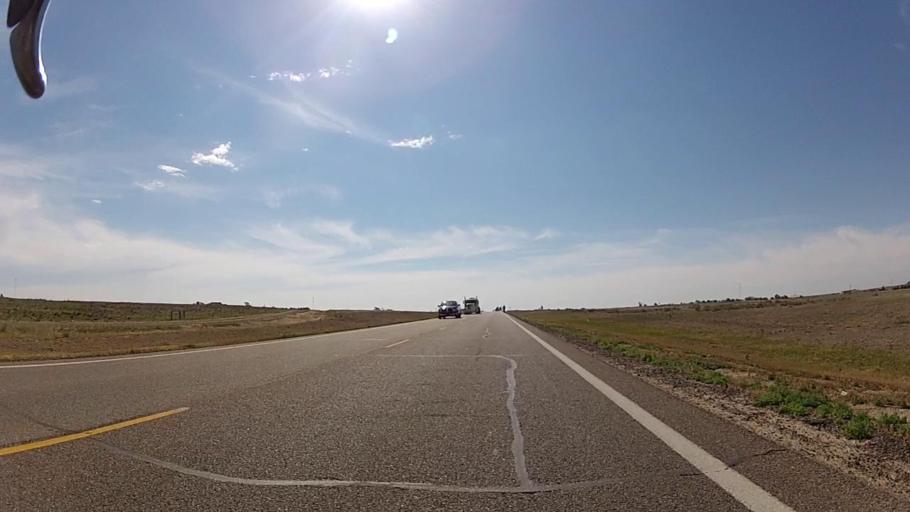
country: US
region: Kansas
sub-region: Grant County
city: Ulysses
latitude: 37.5690
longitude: -101.3256
